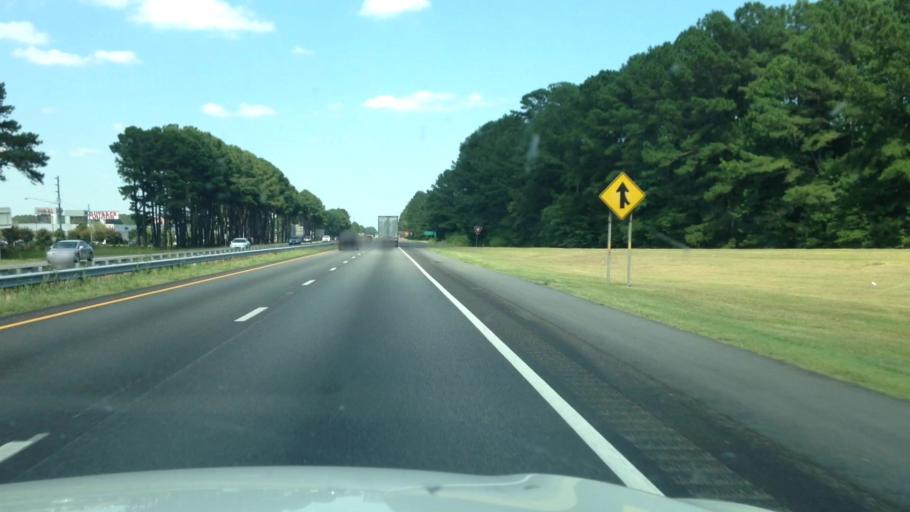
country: US
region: North Carolina
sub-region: Johnston County
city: Smithfield
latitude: 35.5049
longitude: -78.3191
